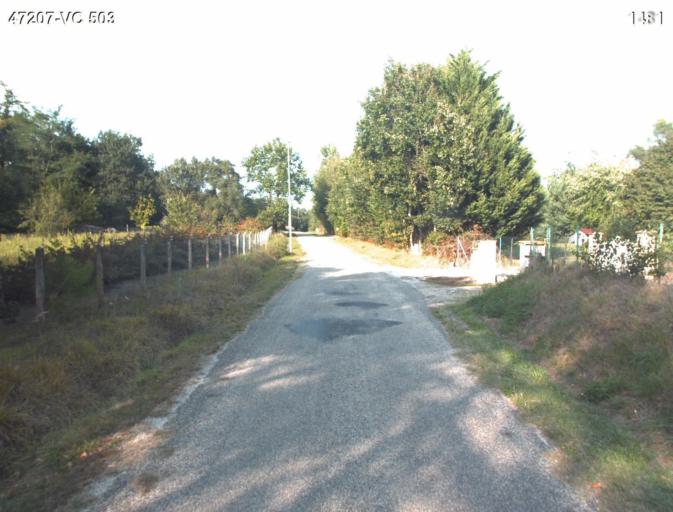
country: FR
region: Aquitaine
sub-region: Departement du Lot-et-Garonne
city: Barbaste
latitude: 44.1938
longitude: 0.2304
